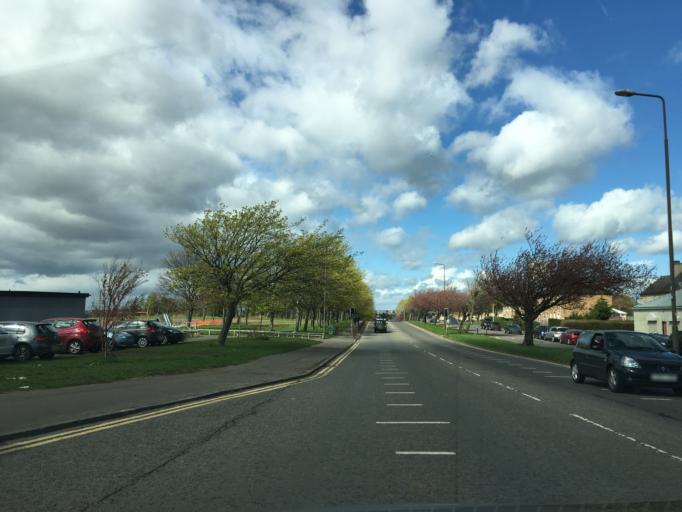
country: GB
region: Scotland
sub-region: Edinburgh
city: Colinton
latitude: 55.9261
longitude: -3.2830
